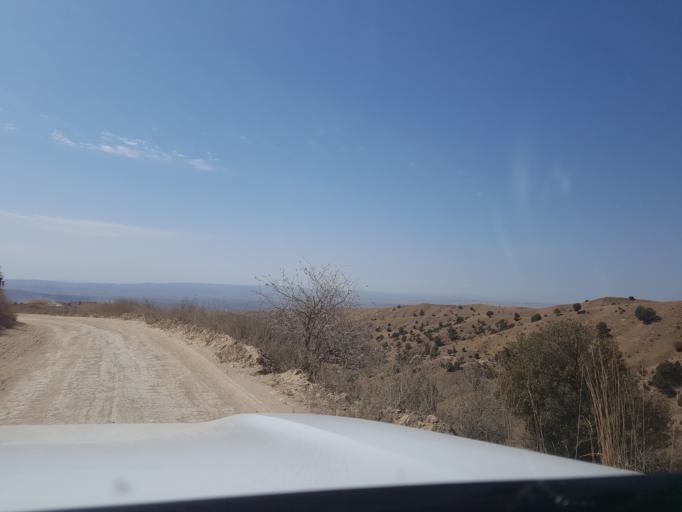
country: TM
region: Ahal
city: Baharly
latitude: 38.2945
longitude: 56.9350
